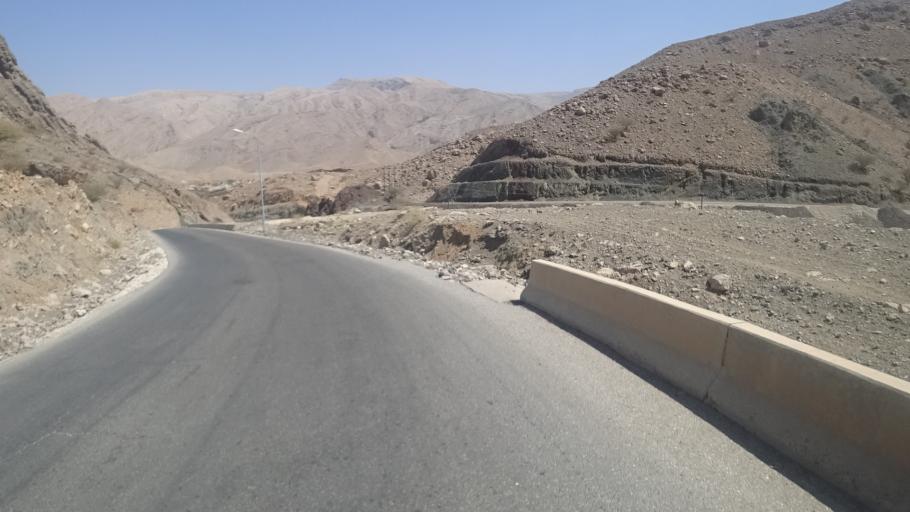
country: OM
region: Ash Sharqiyah
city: Badiyah
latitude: 22.5668
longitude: 59.0841
